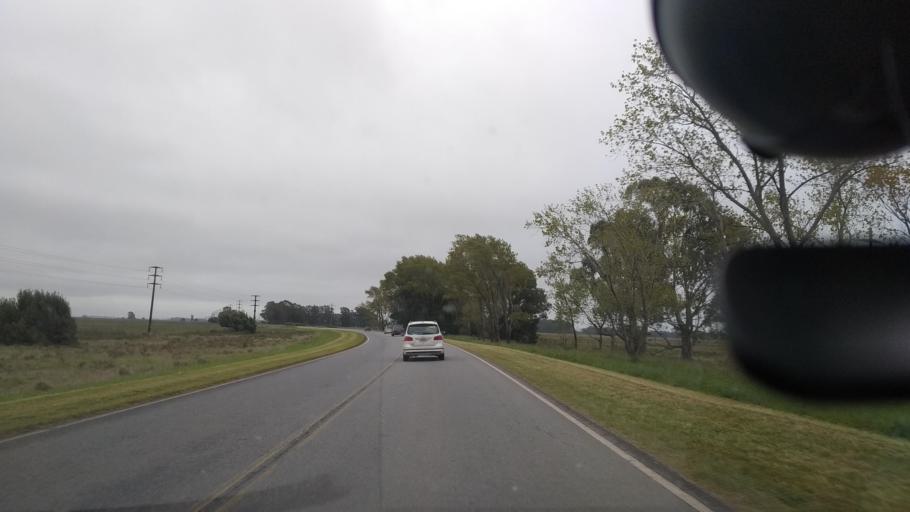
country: AR
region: Buenos Aires
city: Veronica
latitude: -35.3796
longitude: -57.3687
